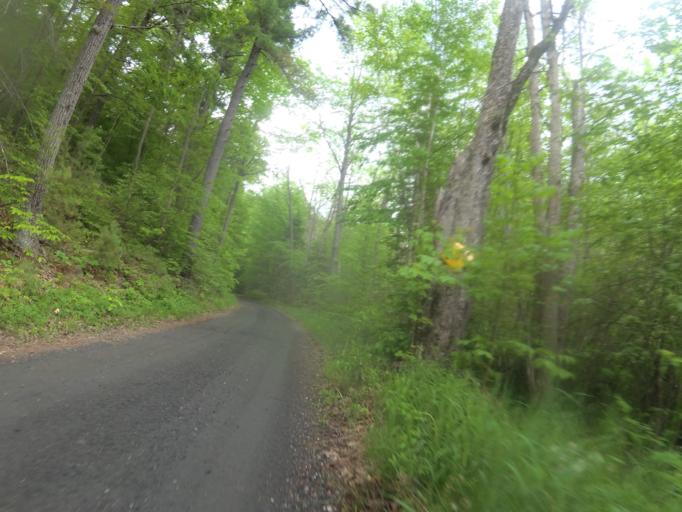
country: CA
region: Ontario
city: Renfrew
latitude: 45.1142
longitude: -76.8227
